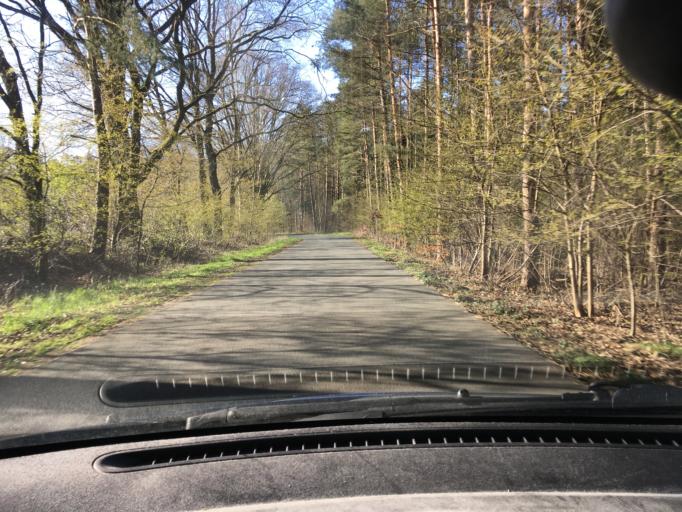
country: DE
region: Lower Saxony
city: Bispingen
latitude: 53.1082
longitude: 10.0463
